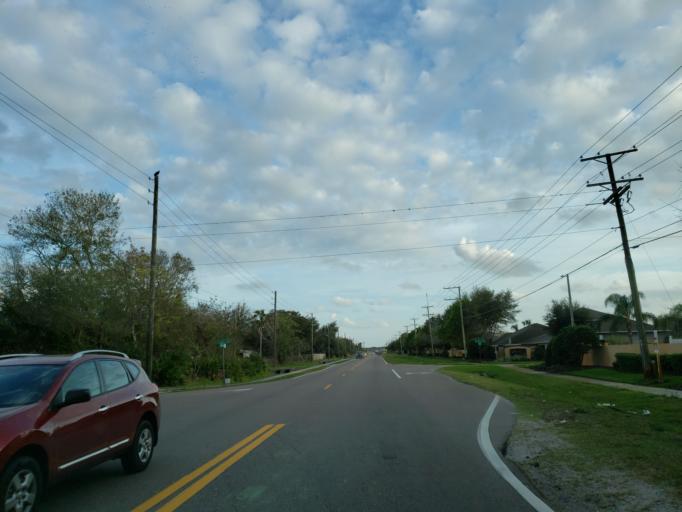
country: US
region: Florida
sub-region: Hillsborough County
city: Balm
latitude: 27.8070
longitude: -82.2900
